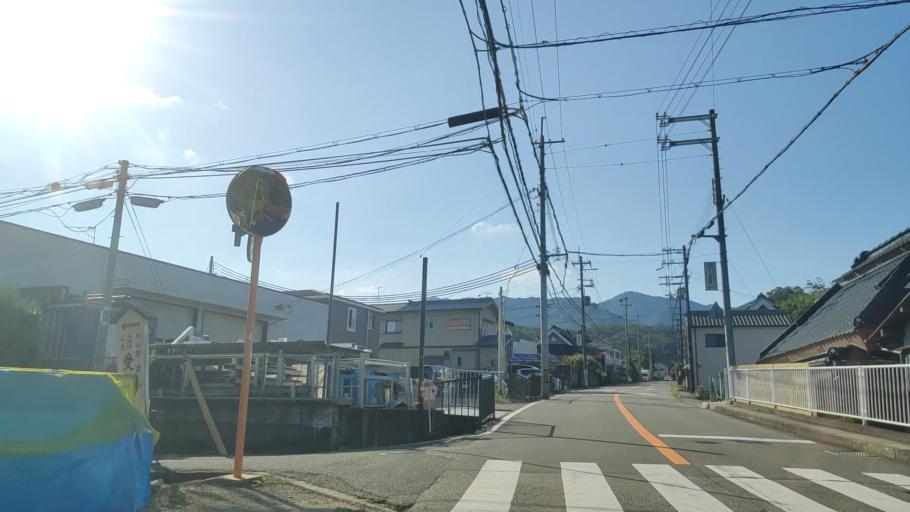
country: JP
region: Hyogo
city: Sandacho
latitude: 34.8122
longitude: 135.2497
